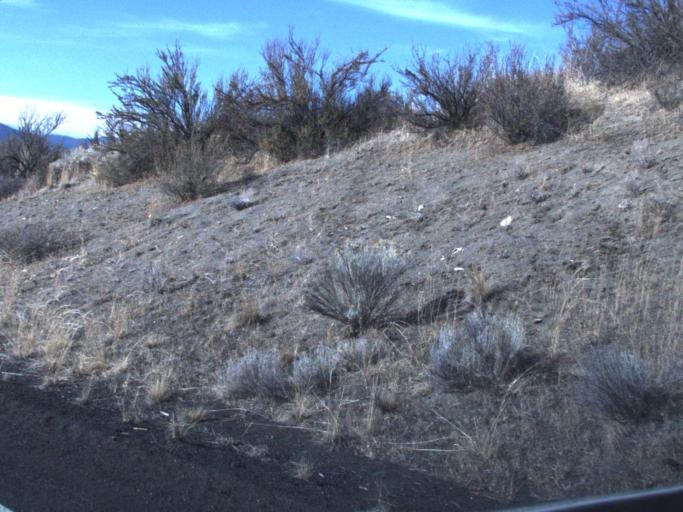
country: US
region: Washington
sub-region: Lincoln County
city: Davenport
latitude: 47.9102
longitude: -118.2774
